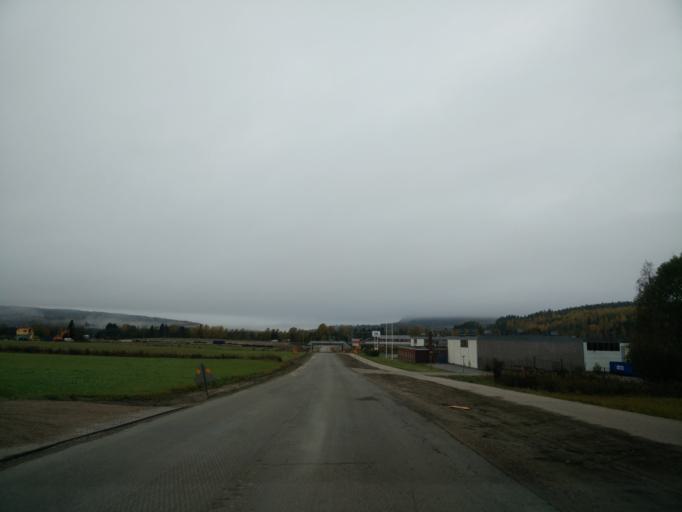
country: SE
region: Vaesternorrland
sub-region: Sundsvalls Kommun
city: Nolby
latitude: 62.2928
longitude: 17.3568
